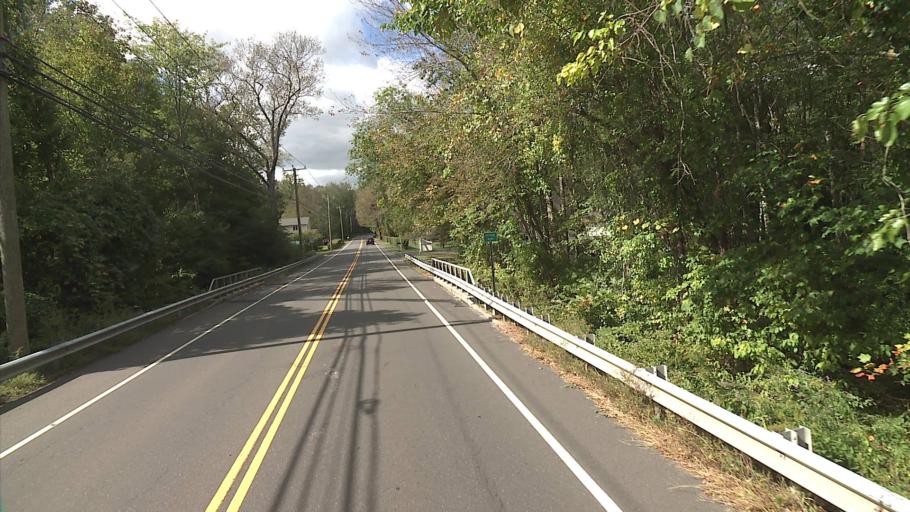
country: US
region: Connecticut
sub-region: Middlesex County
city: Chester Center
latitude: 41.3987
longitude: -72.4800
